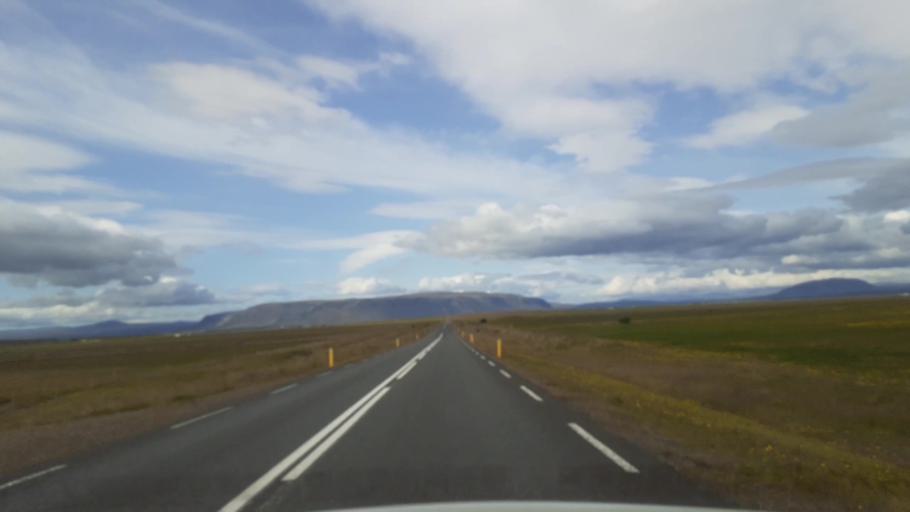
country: IS
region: South
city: Selfoss
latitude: 63.9047
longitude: -20.8154
